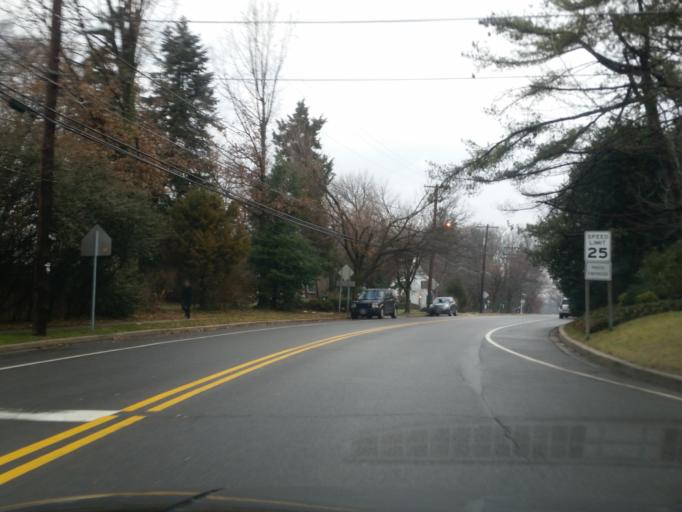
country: US
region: Maryland
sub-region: Montgomery County
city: Chevy Chase
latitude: 38.9854
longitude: -77.0726
